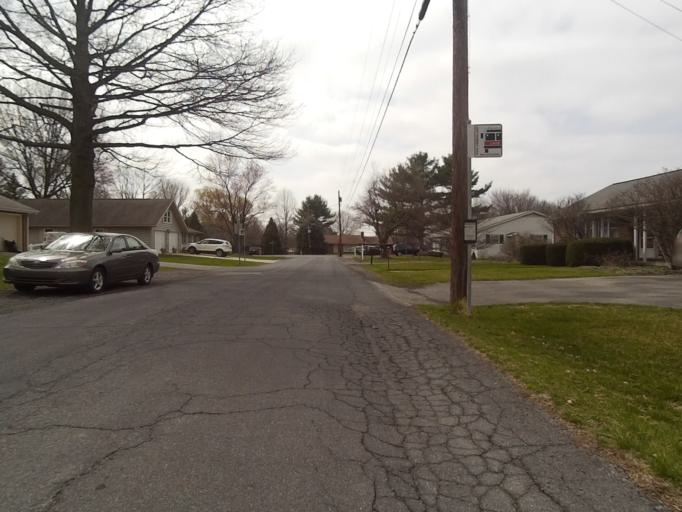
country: US
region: Pennsylvania
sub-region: Centre County
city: Boalsburg
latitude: 40.7869
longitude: -77.7942
